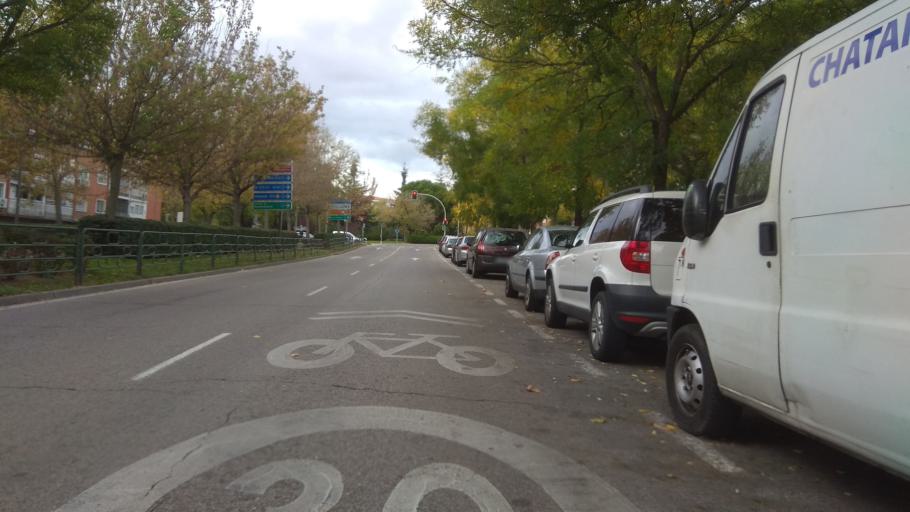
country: ES
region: Madrid
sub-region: Provincia de Madrid
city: Vicalvaro
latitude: 40.4091
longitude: -3.6082
